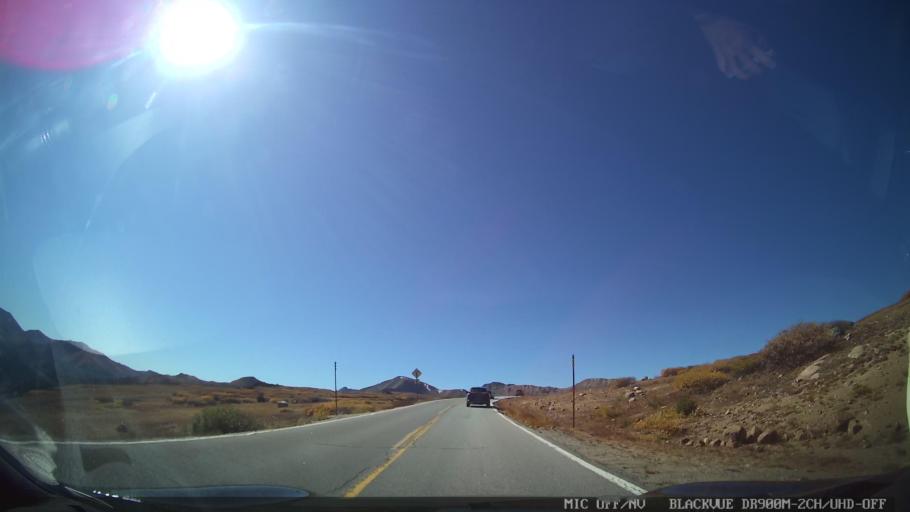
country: US
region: Colorado
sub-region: Pitkin County
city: Aspen
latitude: 39.1103
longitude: -106.5625
